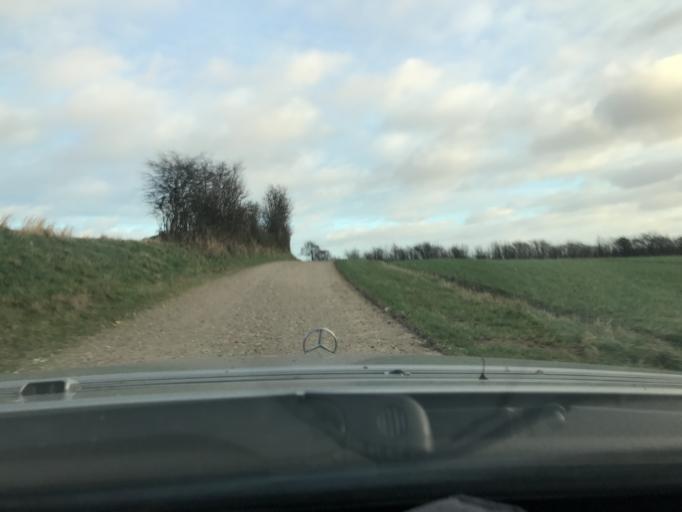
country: DK
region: South Denmark
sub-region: Sonderborg Kommune
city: Nordborg
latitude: 55.0459
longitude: 9.6520
